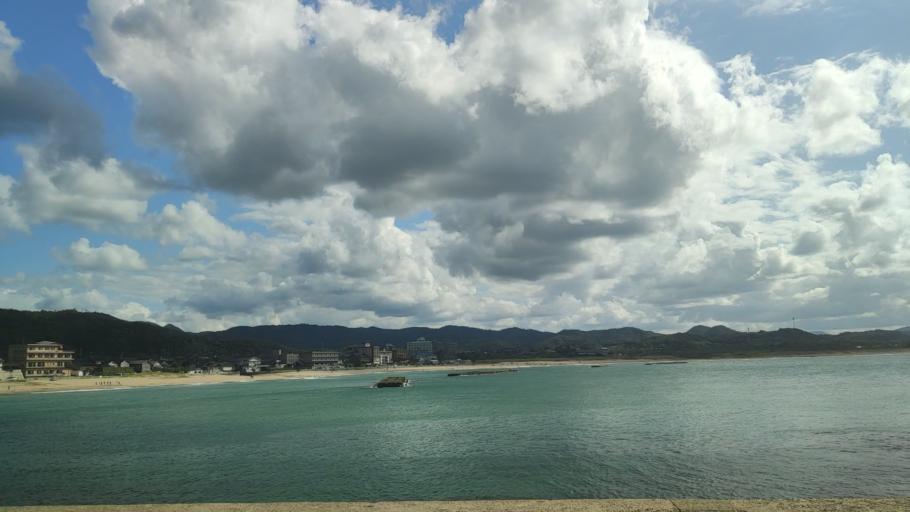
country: JP
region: Hyogo
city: Toyooka
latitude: 35.6708
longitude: 134.9651
